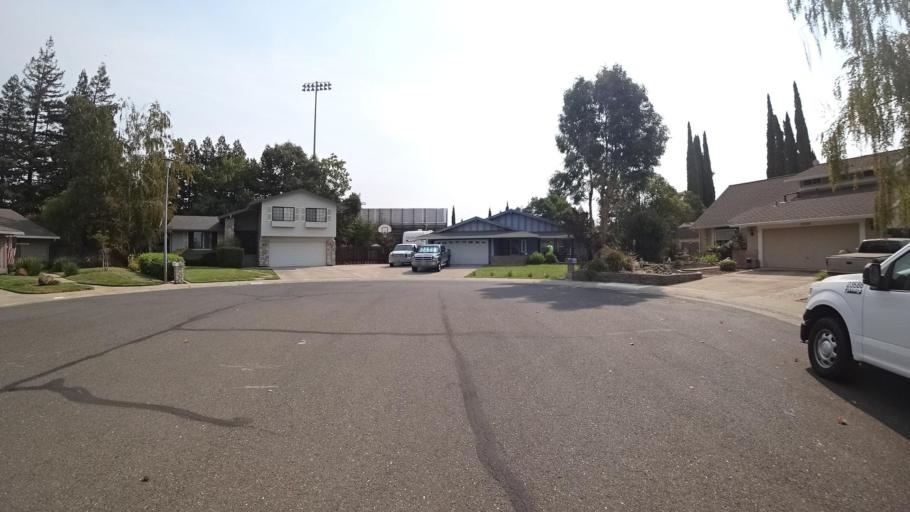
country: US
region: California
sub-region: Sacramento County
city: Elk Grove
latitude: 38.3987
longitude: -121.3760
